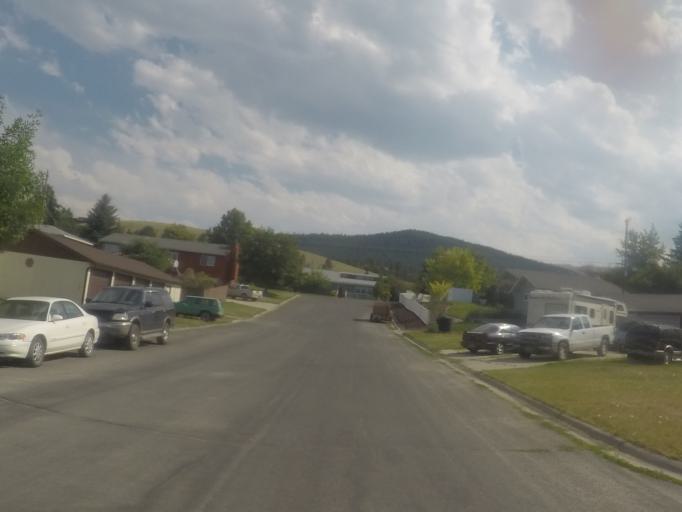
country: US
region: Montana
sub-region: Lewis and Clark County
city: Helena
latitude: 46.5823
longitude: -112.0071
